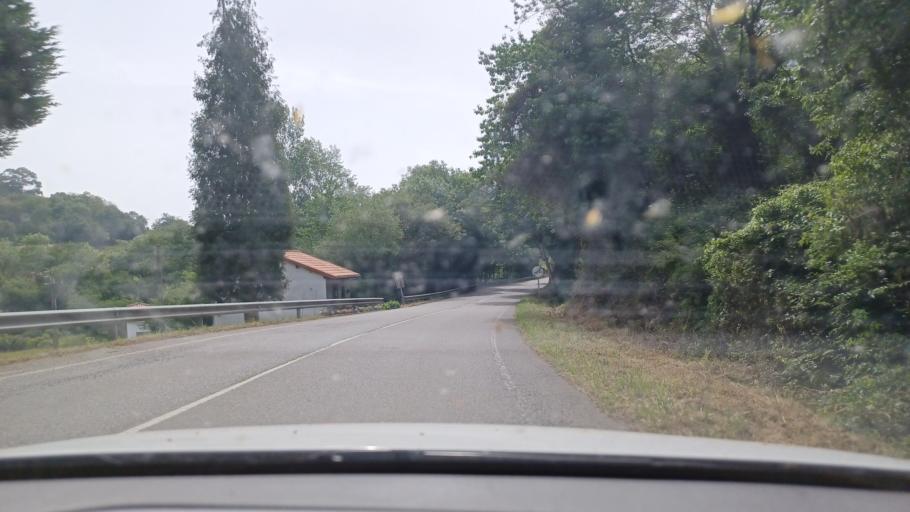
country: ES
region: Asturias
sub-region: Province of Asturias
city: Ribadesella
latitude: 43.4416
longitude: -4.9865
